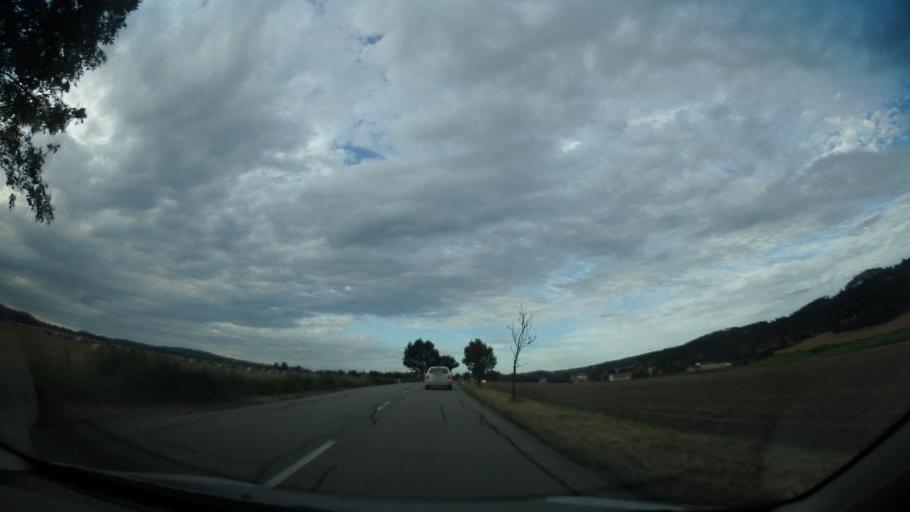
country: CZ
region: South Moravian
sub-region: Okres Blansko
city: Boskovice
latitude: 49.5247
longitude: 16.6825
